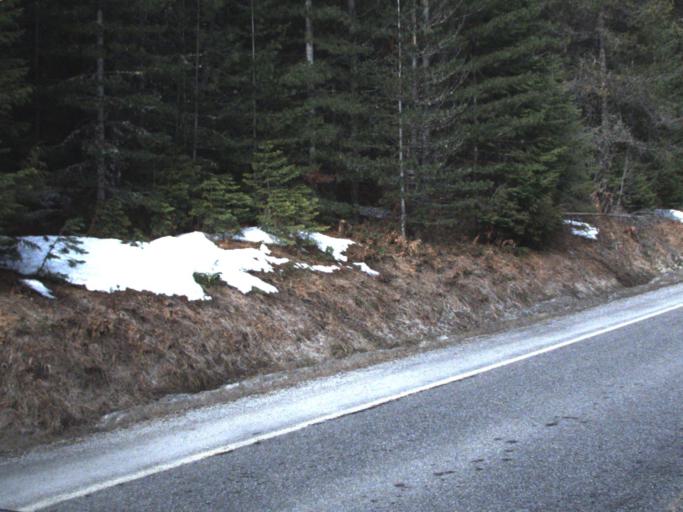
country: US
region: Washington
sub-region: Pend Oreille County
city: Newport
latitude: 48.4470
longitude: -117.3232
